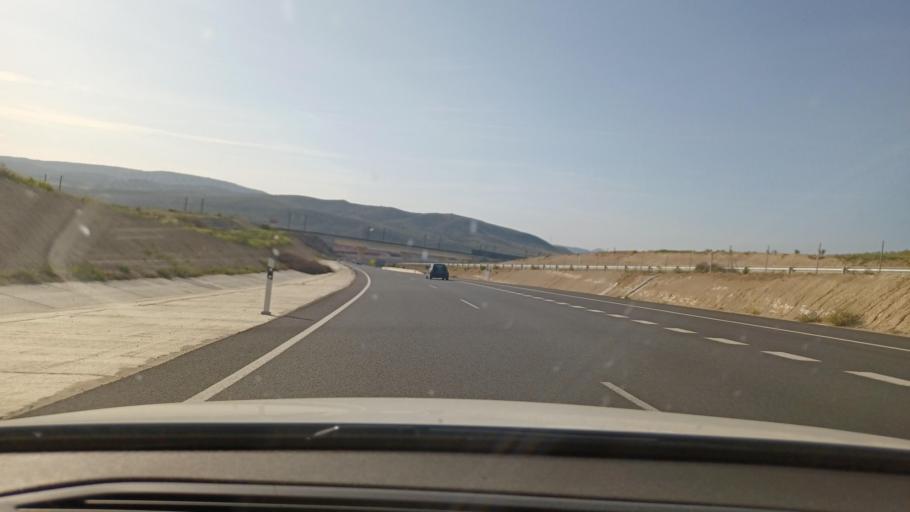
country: ES
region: Castille-La Mancha
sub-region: Provincia de Albacete
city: Caudete
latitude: 38.7211
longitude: -0.9366
